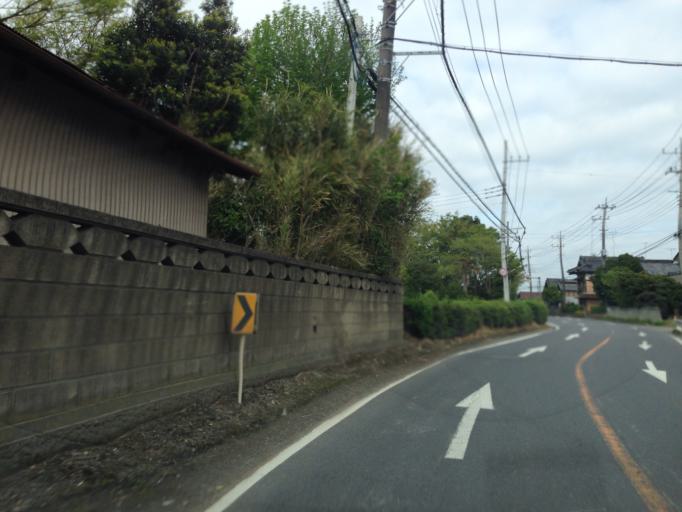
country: JP
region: Ibaraki
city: Tsukuba
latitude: 36.1376
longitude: 140.0545
